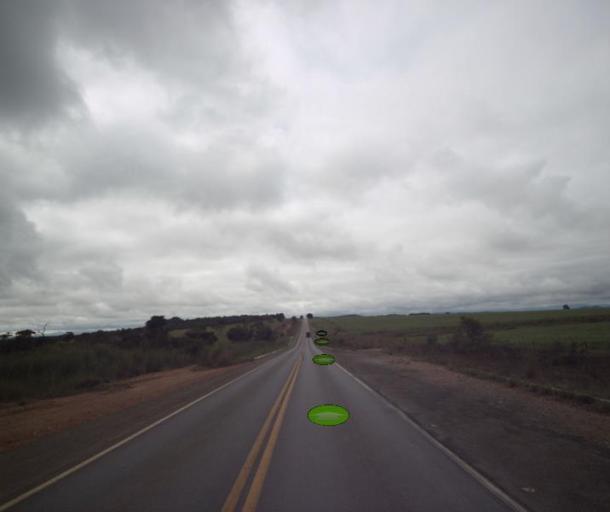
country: BR
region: Goias
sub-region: Uruacu
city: Uruacu
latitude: -14.6569
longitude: -49.1614
